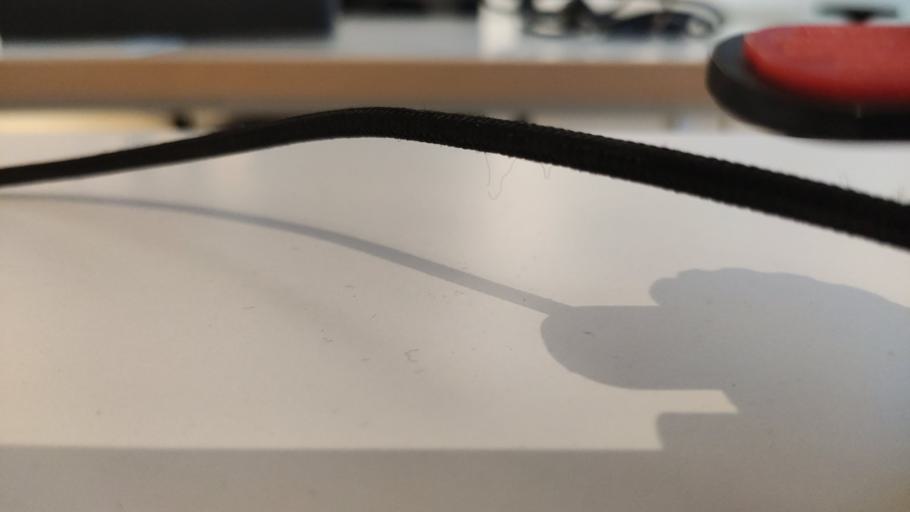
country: RU
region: Moskovskaya
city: Sychevo
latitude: 55.8203
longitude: 36.3055
